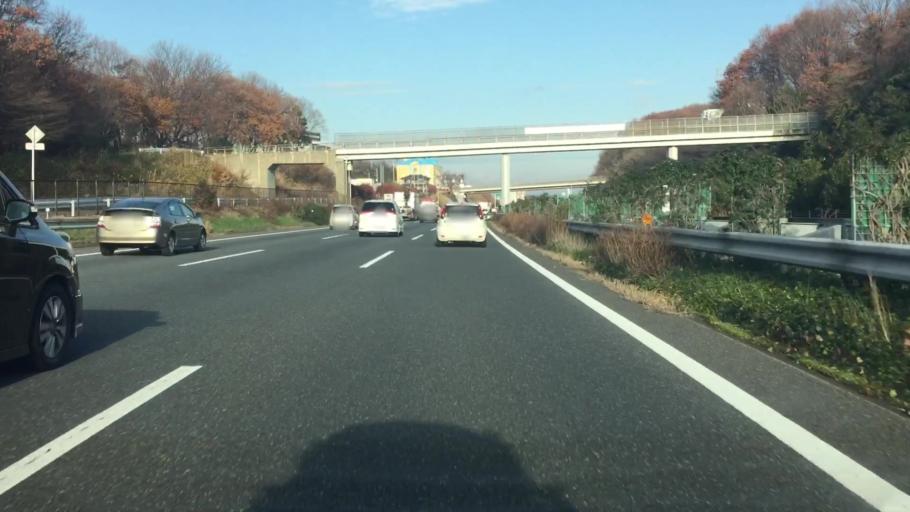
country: JP
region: Saitama
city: Honjo
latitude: 36.2088
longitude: 139.1711
